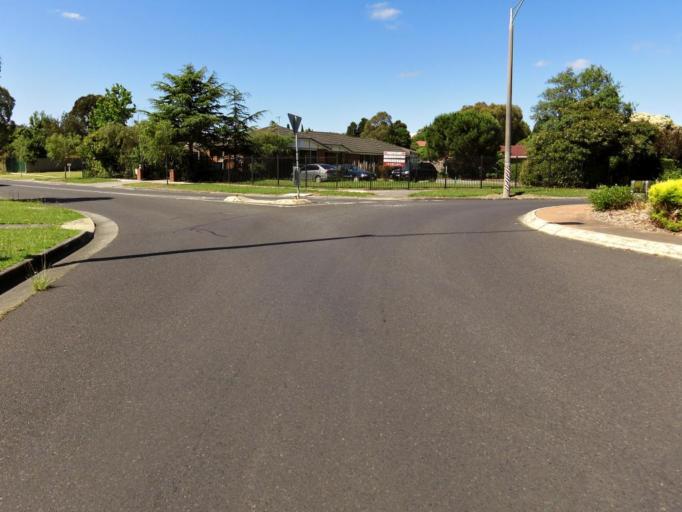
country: AU
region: Victoria
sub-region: Casey
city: Endeavour Hills
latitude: -37.9659
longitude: 145.2628
